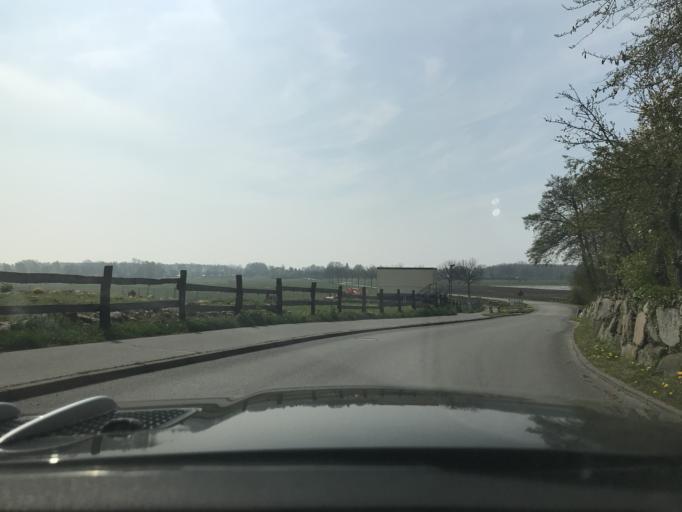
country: DE
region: Schleswig-Holstein
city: Gromitz
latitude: 54.1657
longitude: 10.9838
